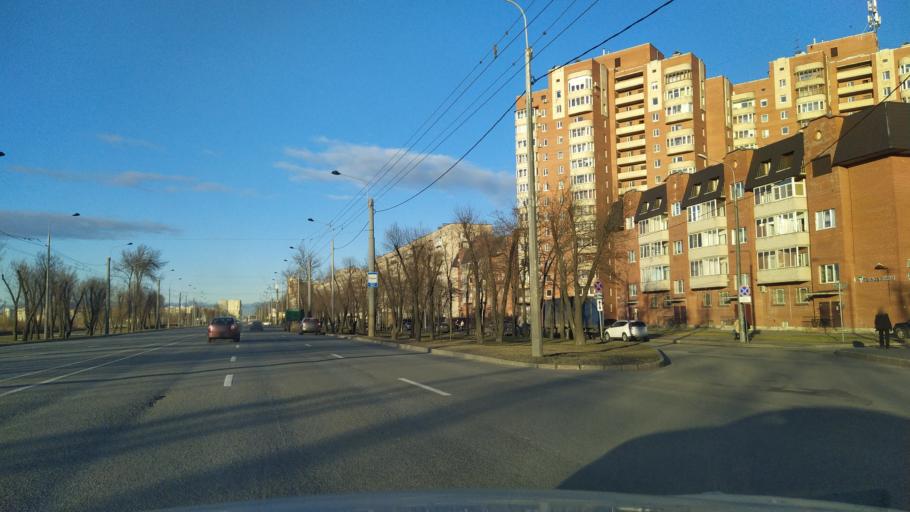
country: RU
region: St.-Petersburg
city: Uritsk
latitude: 59.8339
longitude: 30.1959
